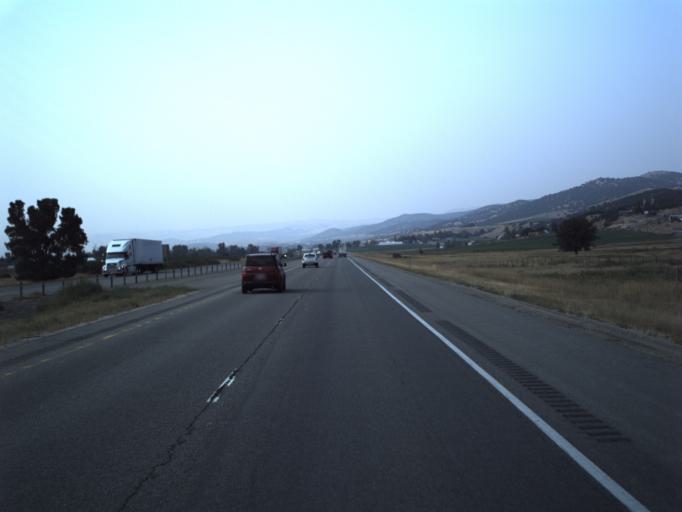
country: US
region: Utah
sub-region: Summit County
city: Coalville
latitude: 40.8302
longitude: -111.3908
